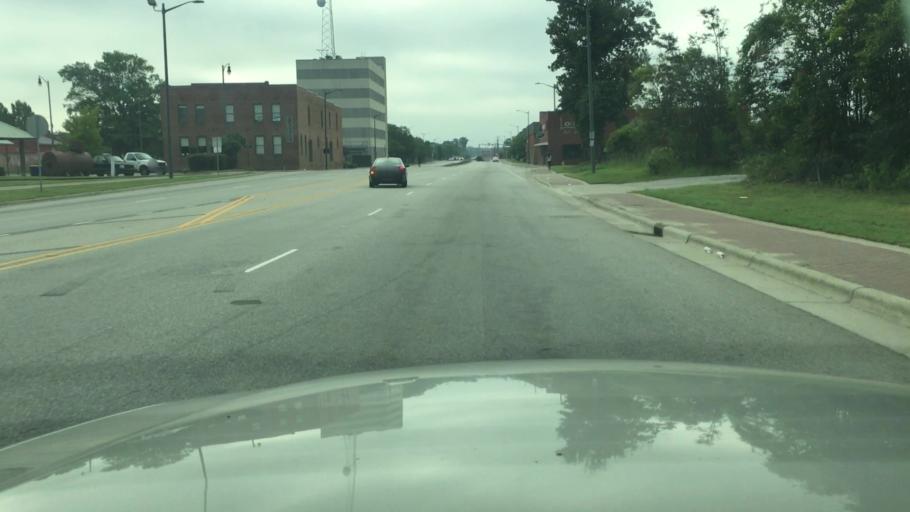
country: US
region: North Carolina
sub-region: Cumberland County
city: Fayetteville
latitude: 35.0518
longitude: -78.8828
